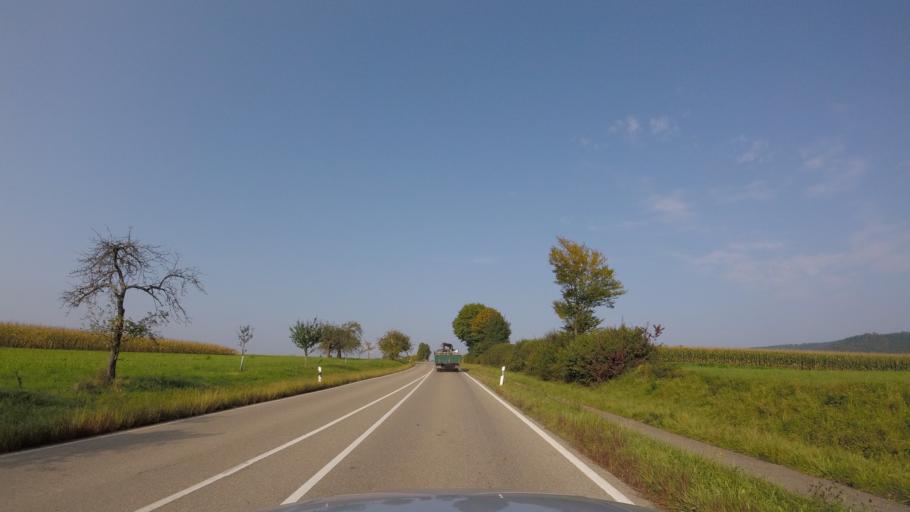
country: DE
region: Baden-Wuerttemberg
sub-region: Regierungsbezirk Stuttgart
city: Aspach
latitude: 48.9906
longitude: 9.4033
